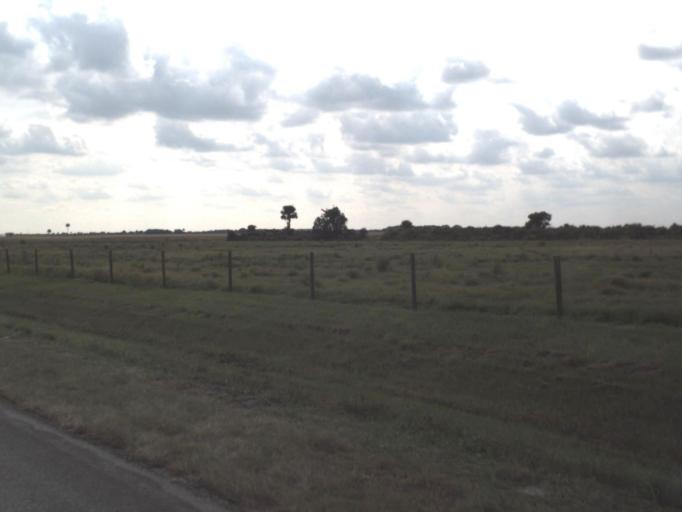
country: US
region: Florida
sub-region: Okeechobee County
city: Cypress Quarters
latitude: 27.4813
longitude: -80.8071
